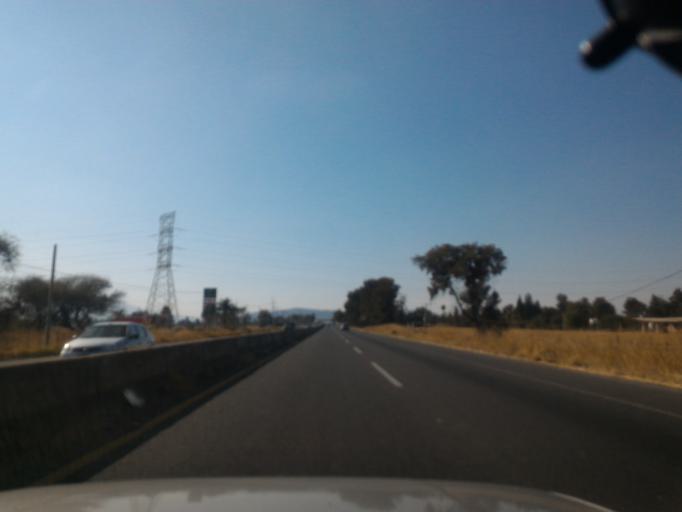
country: MX
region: Jalisco
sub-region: Ixtlahuacan de los Membrillos
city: Valle de los Girasoles [Fraccionamiento]
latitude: 20.4061
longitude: -103.1883
